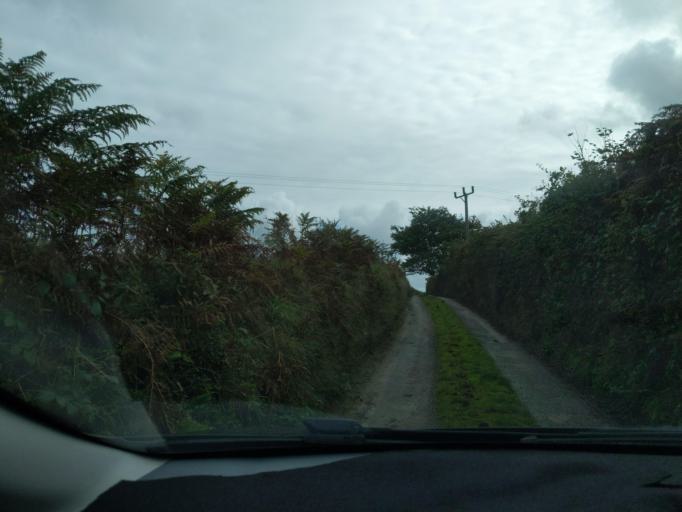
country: GB
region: England
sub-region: Cornwall
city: Par
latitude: 50.3899
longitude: -4.7034
